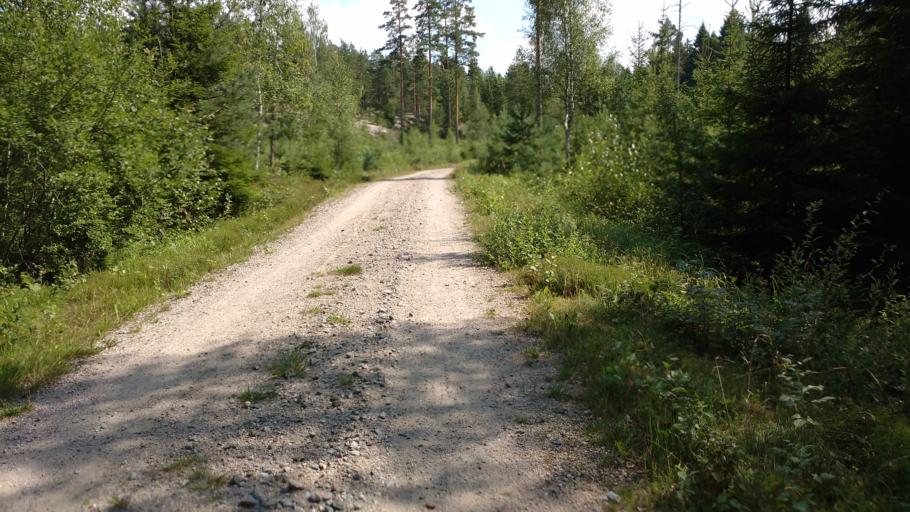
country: FI
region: Varsinais-Suomi
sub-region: Salo
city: Pertteli
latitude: 60.4043
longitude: 23.2104
